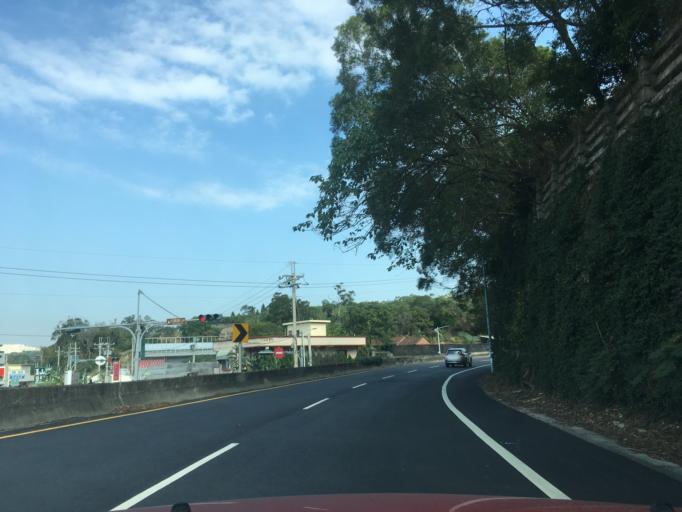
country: TW
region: Taiwan
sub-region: Hsinchu
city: Hsinchu
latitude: 24.7596
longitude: 121.0058
